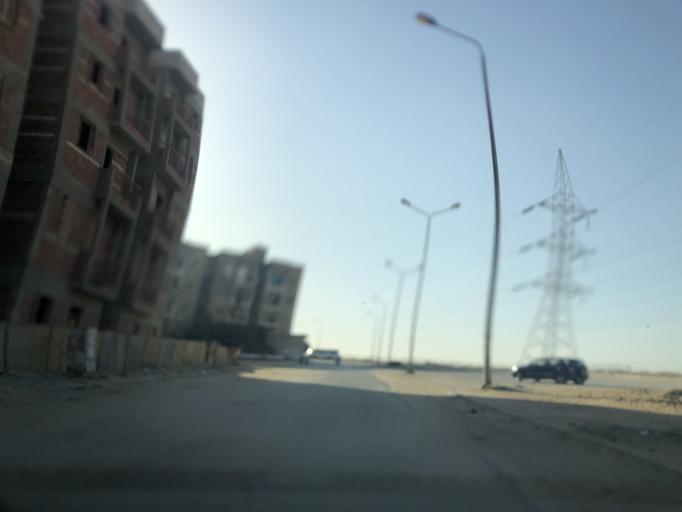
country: EG
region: Al Jizah
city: Al Jizah
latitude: 29.9881
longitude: 31.1085
